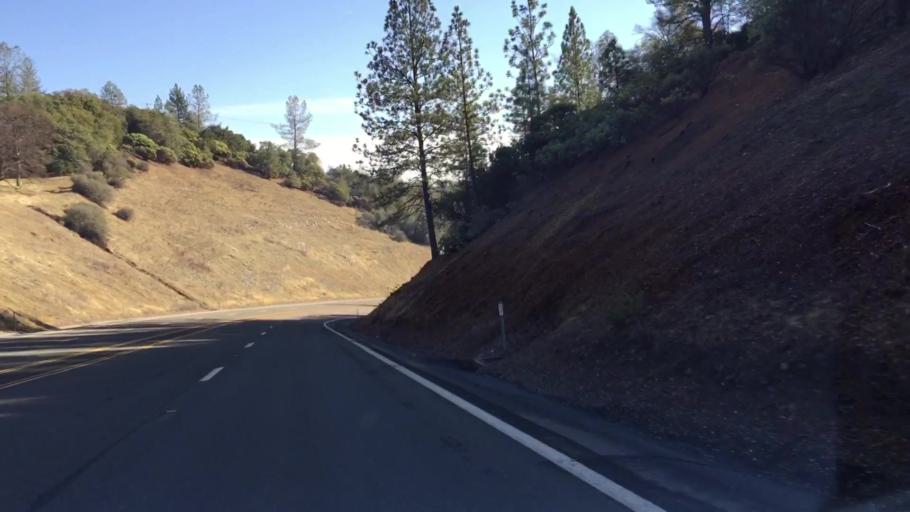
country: US
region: California
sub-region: Butte County
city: Berry Creek
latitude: 39.6727
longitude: -121.5281
